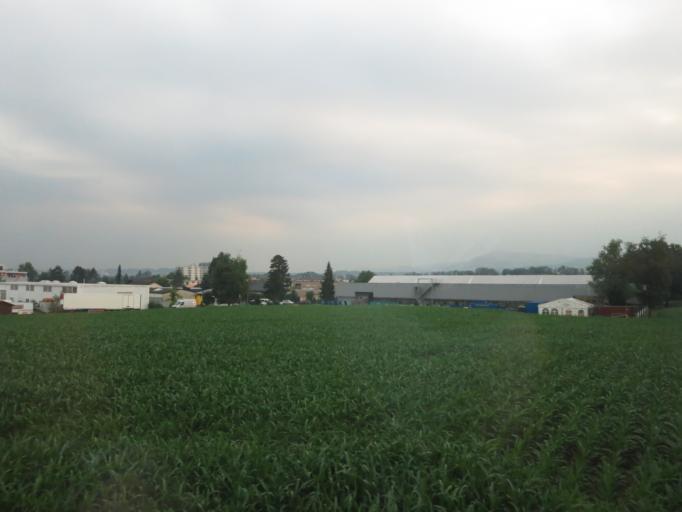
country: CH
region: Schwyz
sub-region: Bezirk March
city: Lachen
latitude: 47.1916
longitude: 8.8624
